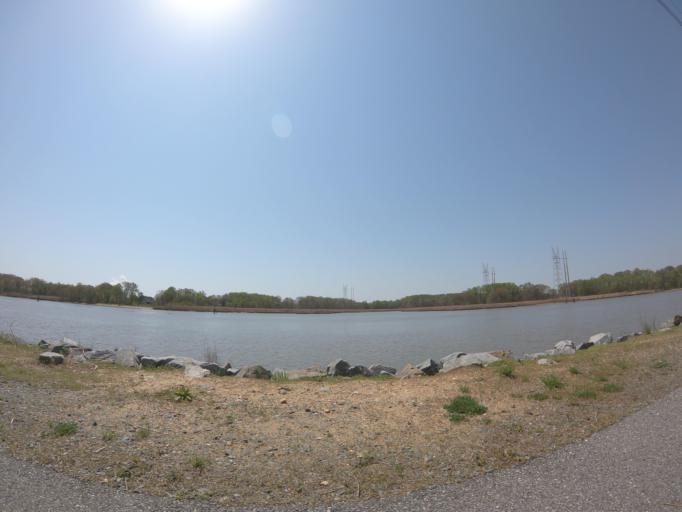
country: US
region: Delaware
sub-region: New Castle County
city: Delaware City
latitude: 39.5554
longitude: -75.6193
